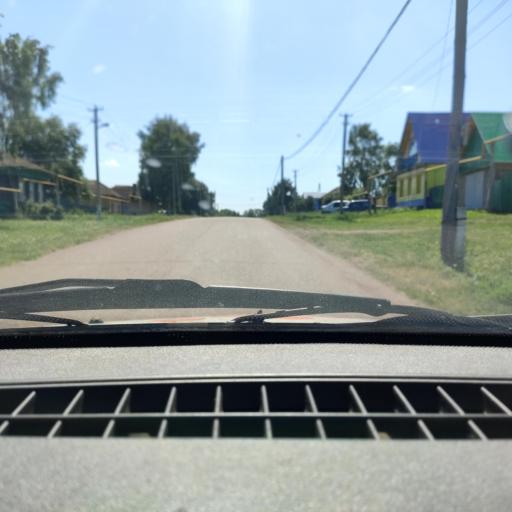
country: RU
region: Bashkortostan
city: Blagoveshchensk
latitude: 55.0992
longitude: 55.8544
